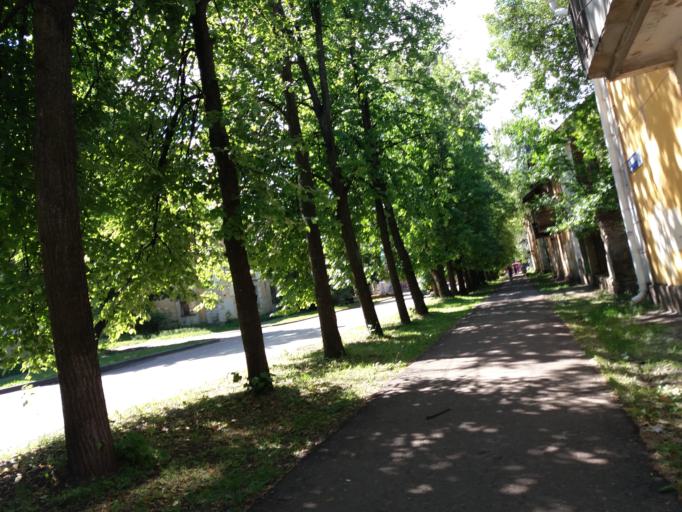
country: RU
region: Jaroslavl
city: Yaroslavl
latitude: 57.6391
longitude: 39.8397
